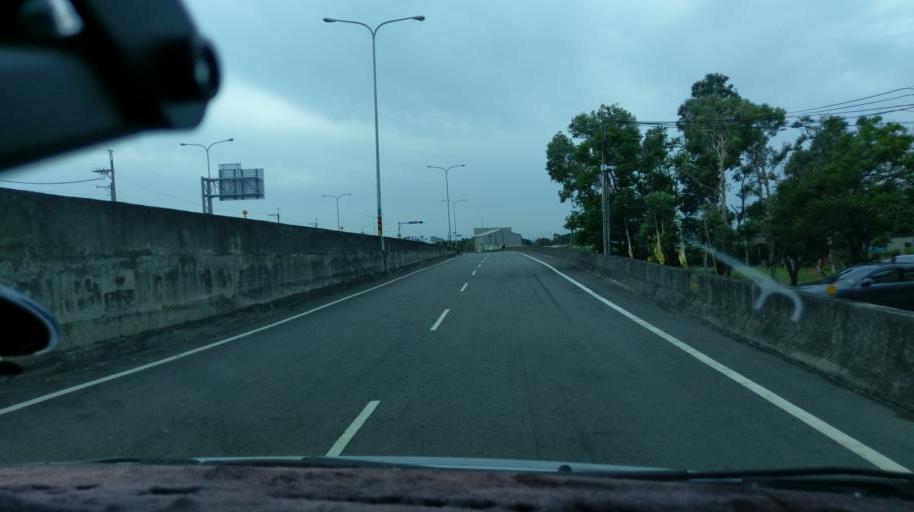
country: TW
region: Taiwan
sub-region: Hsinchu
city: Hsinchu
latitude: 24.7145
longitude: 120.8671
